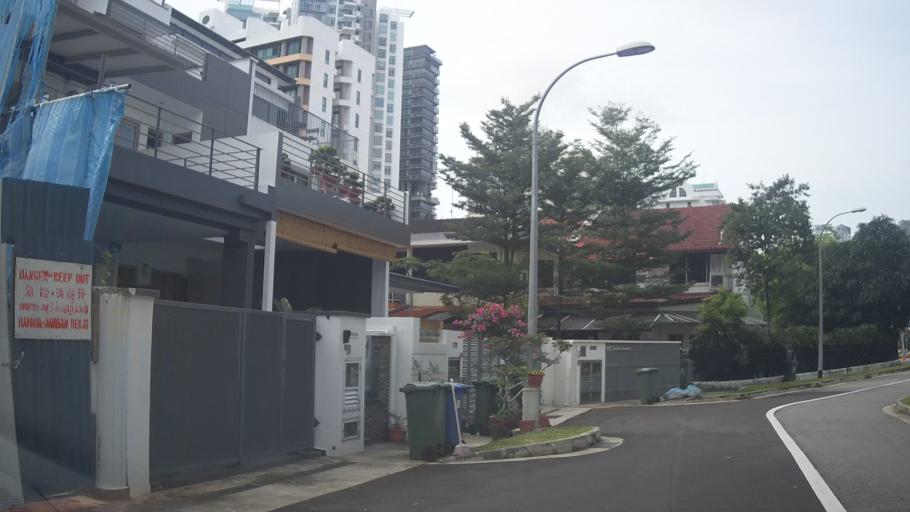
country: SG
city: Singapore
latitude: 1.3267
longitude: 103.8647
